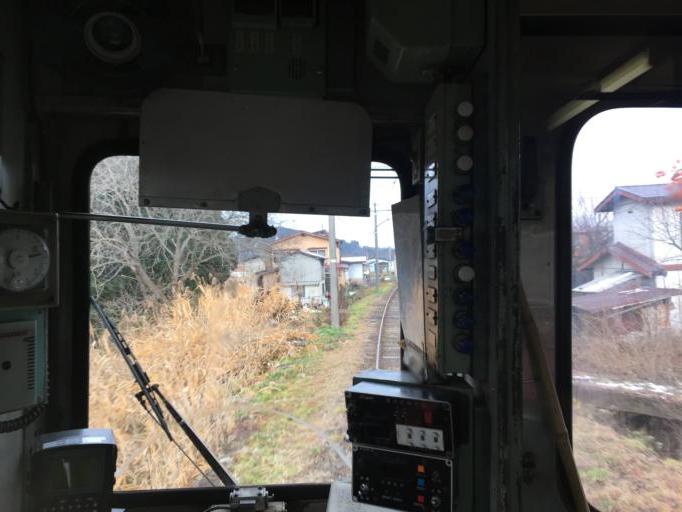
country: JP
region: Aomori
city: Hirosaki
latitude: 40.5242
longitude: 140.5583
